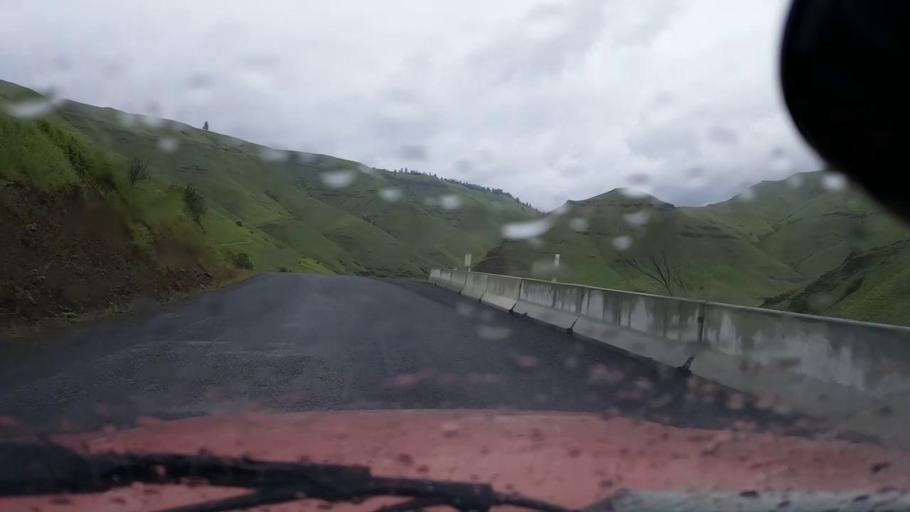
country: US
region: Washington
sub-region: Asotin County
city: Asotin
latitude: 46.0333
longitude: -117.2941
